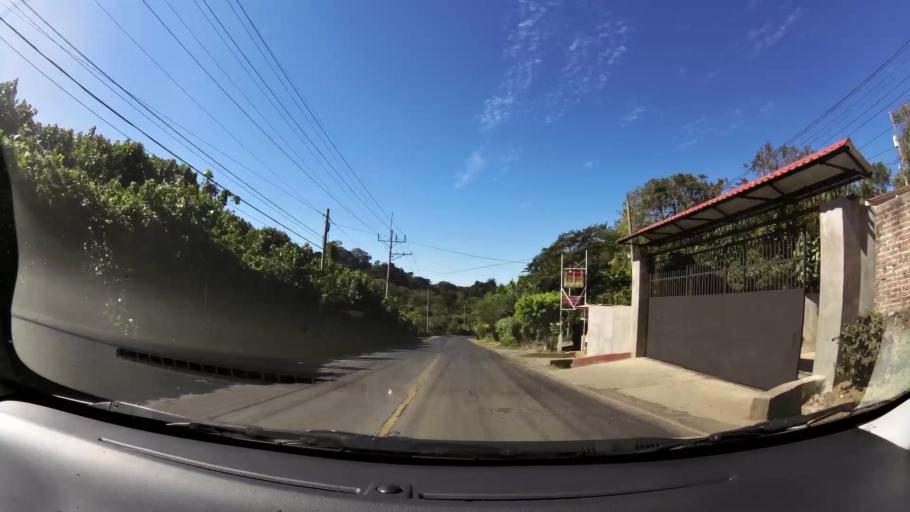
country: SV
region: Ahuachapan
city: Concepcion de Ataco
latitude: 13.8492
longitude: -89.8239
